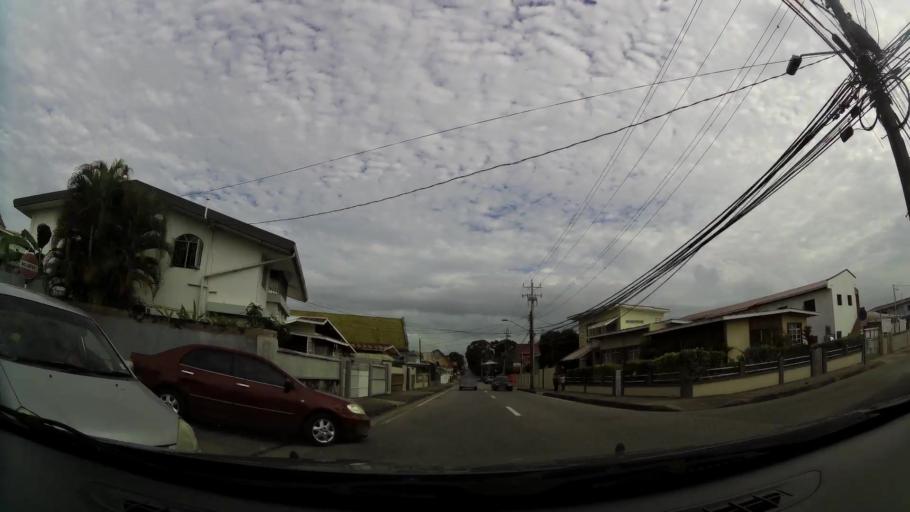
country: TT
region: City of Port of Spain
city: Port-of-Spain
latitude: 10.6650
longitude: -61.5236
